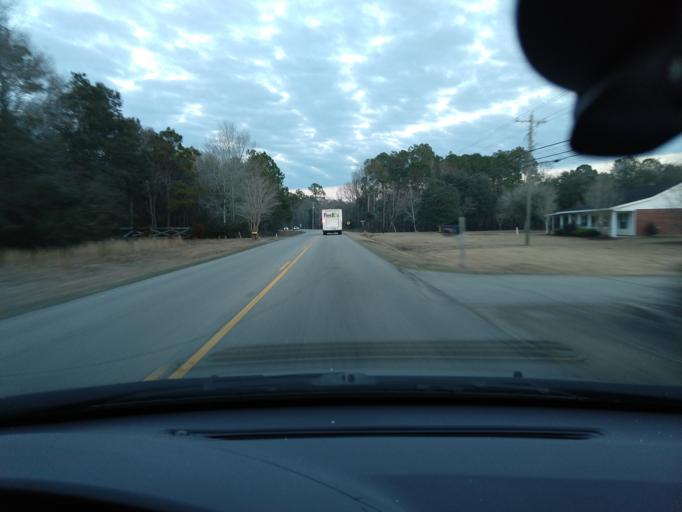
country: US
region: Mississippi
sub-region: Jackson County
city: Gulf Park Estates
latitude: 30.4276
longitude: -88.7432
